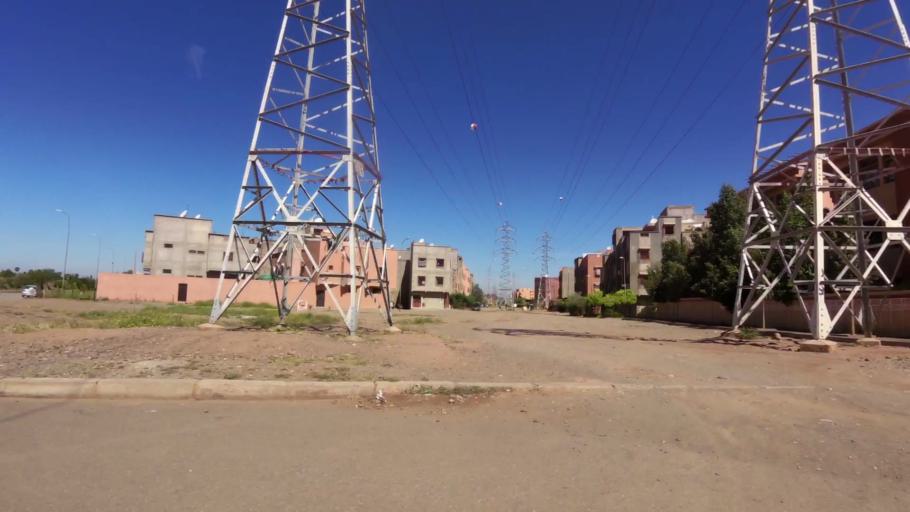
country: MA
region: Marrakech-Tensift-Al Haouz
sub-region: Marrakech
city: Marrakesh
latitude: 31.5706
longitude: -8.0591
